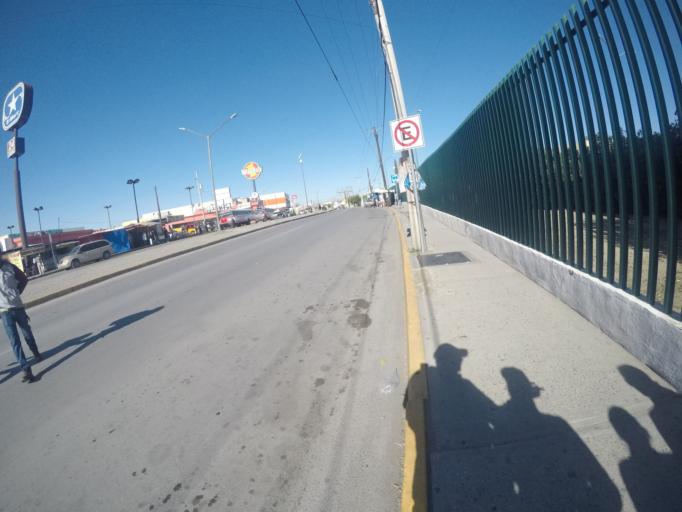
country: US
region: Texas
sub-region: El Paso County
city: Socorro
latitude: 31.6668
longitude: -106.4033
